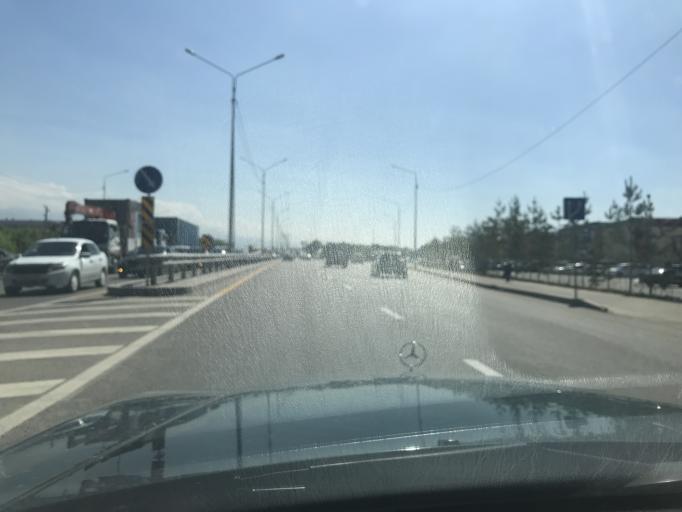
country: KZ
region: Almaty Qalasy
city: Almaty
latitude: 43.3000
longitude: 77.0048
